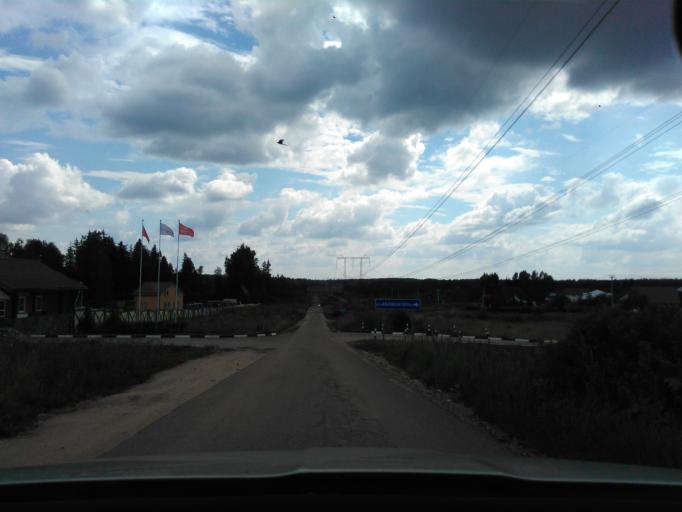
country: RU
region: Moskovskaya
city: Mendeleyevo
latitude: 56.0940
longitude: 37.2699
